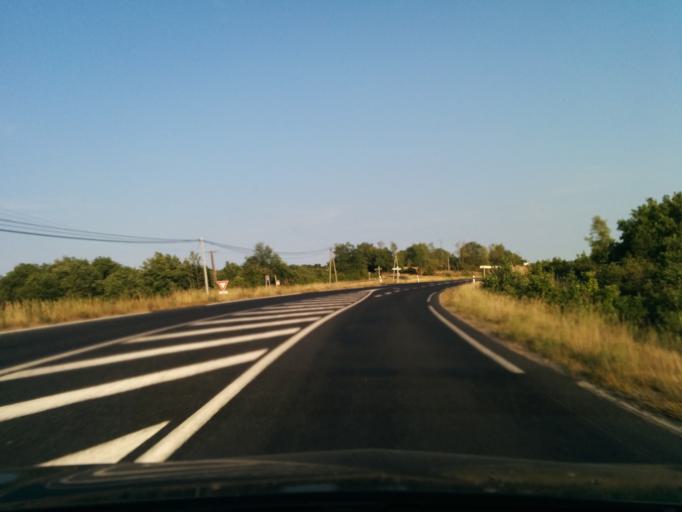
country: FR
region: Midi-Pyrenees
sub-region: Departement du Lot
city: Le Vigan
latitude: 44.7598
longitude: 1.4903
